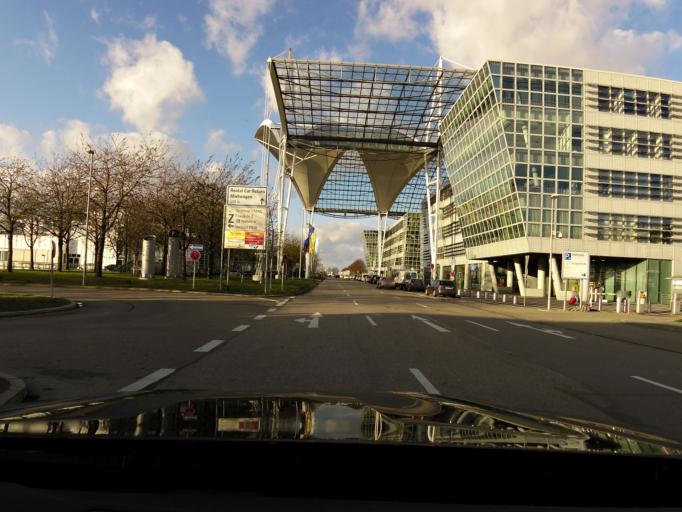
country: DE
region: Bavaria
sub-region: Upper Bavaria
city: Hallbergmoos
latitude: 48.3526
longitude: 11.7873
